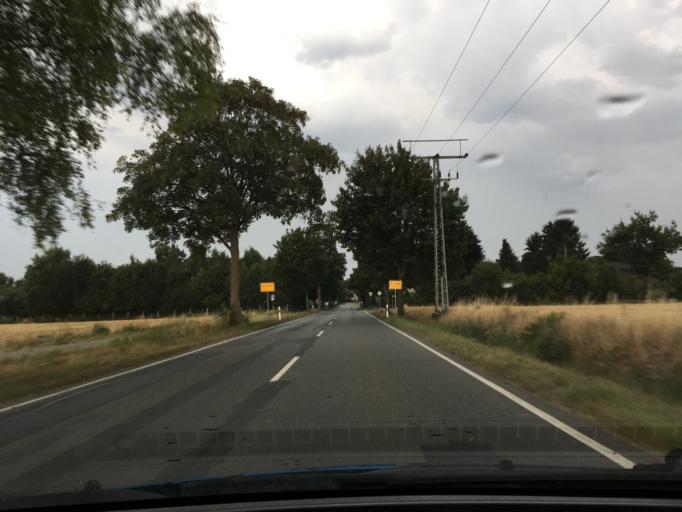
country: DE
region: Lower Saxony
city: Wriedel
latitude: 53.0342
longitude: 10.3065
